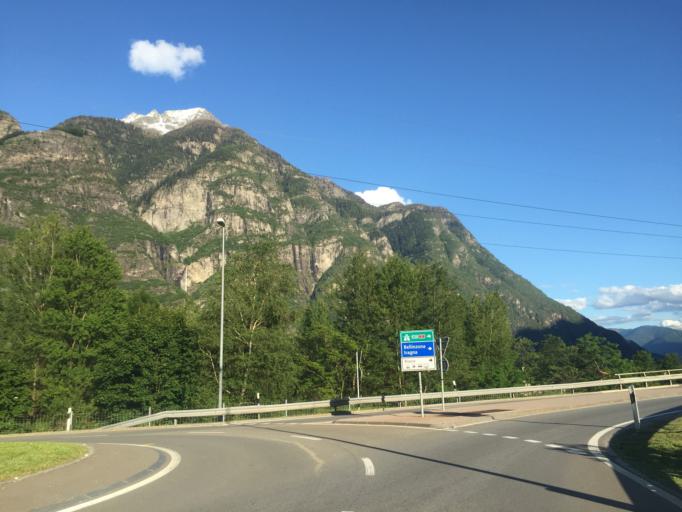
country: CH
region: Ticino
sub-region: Riviera District
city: Biasca
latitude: 46.3587
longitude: 8.9579
